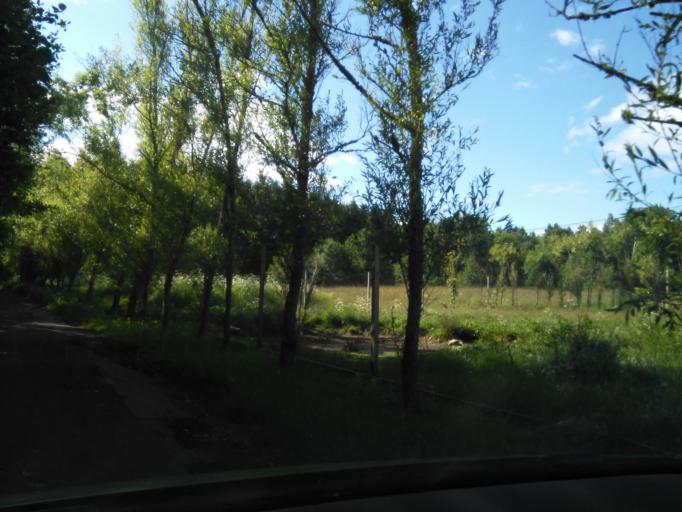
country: DK
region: Capital Region
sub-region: Bornholm Kommune
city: Nexo
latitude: 55.0838
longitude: 15.0752
